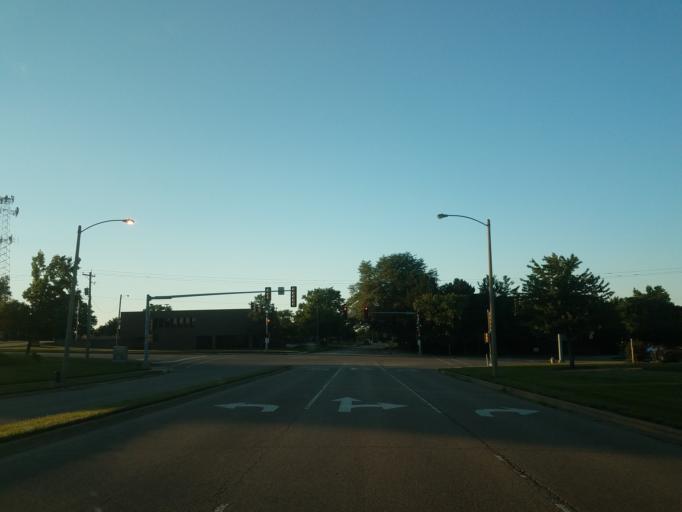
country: US
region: Illinois
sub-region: McLean County
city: Bloomington
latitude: 40.4656
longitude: -88.9501
